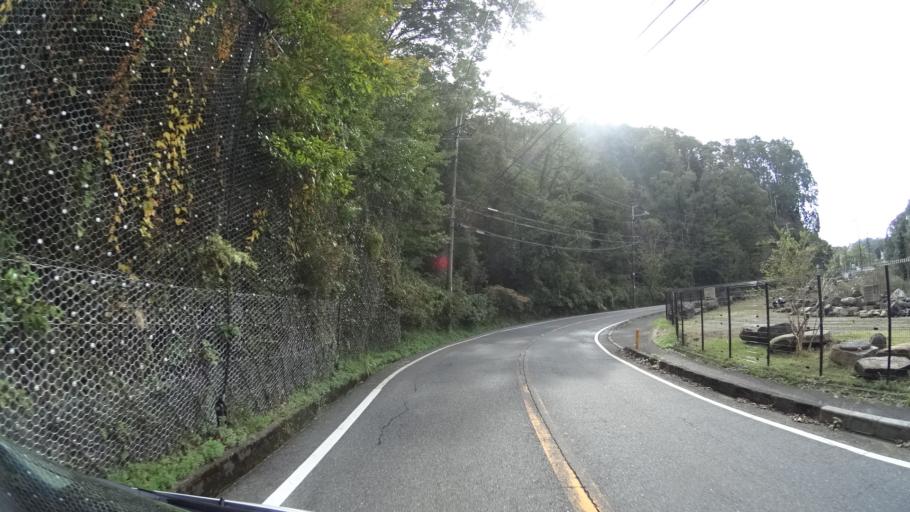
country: JP
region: Shiga Prefecture
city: Otsu-shi
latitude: 35.0383
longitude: 135.8278
